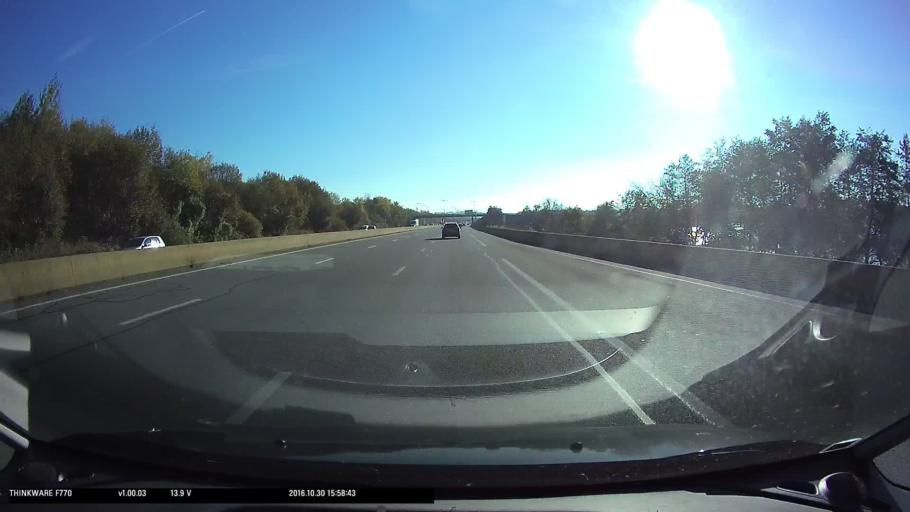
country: FR
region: Franche-Comte
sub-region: Departement du Doubs
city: Nommay
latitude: 47.5326
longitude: 6.8600
